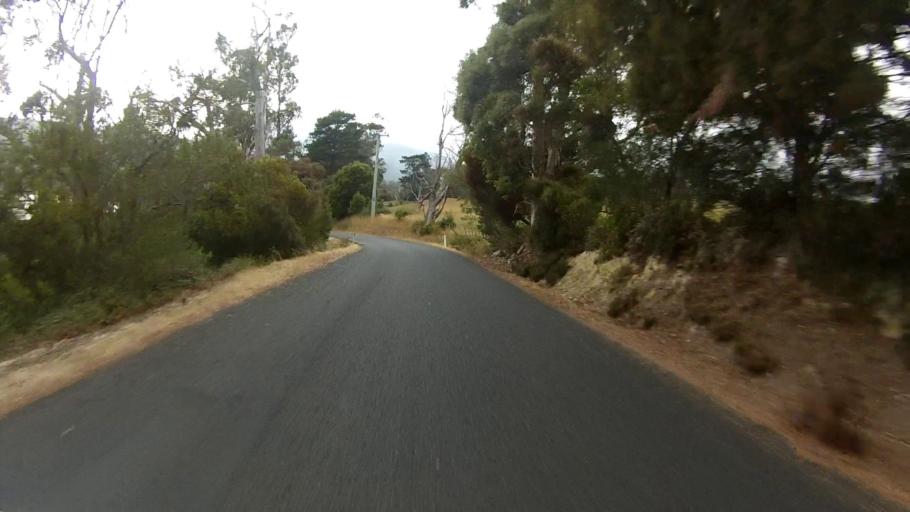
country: AU
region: Tasmania
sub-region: Huon Valley
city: Cygnet
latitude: -43.2148
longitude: 147.1064
